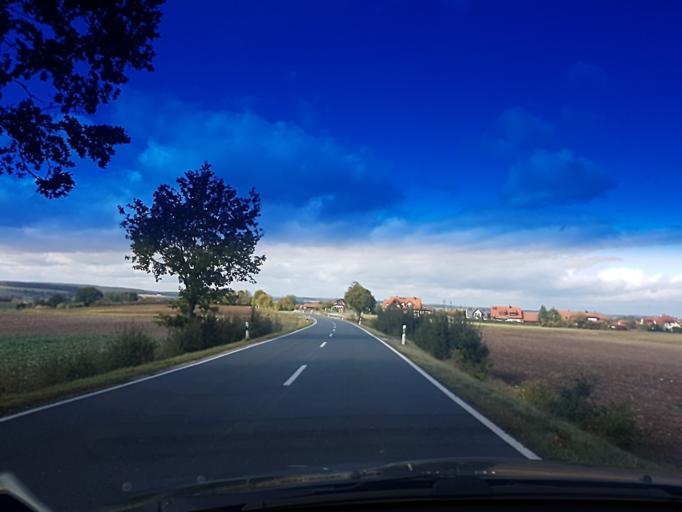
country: DE
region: Bavaria
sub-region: Upper Franconia
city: Pommersfelden
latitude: 49.7480
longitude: 10.8150
